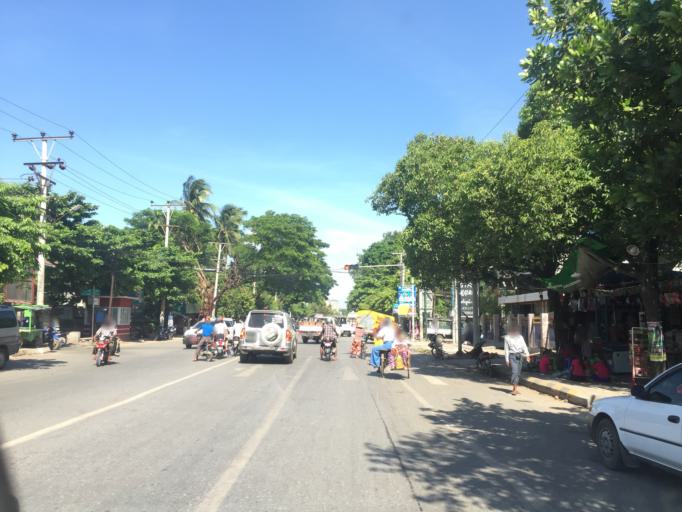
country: MM
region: Mandalay
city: Mandalay
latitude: 21.9839
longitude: 96.0715
